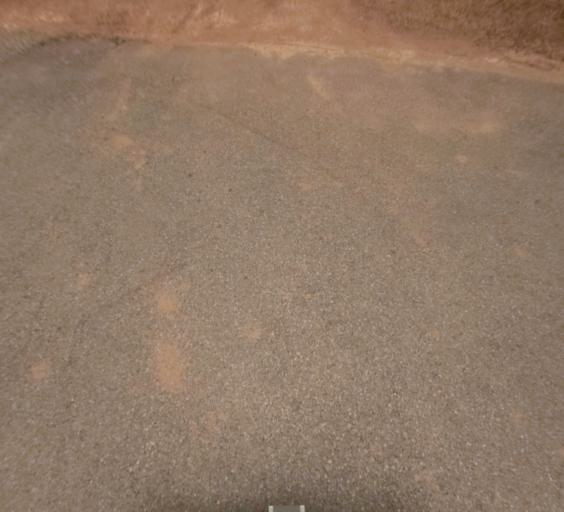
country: US
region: California
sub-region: Madera County
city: Oakhurst
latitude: 37.3674
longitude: -119.6240
